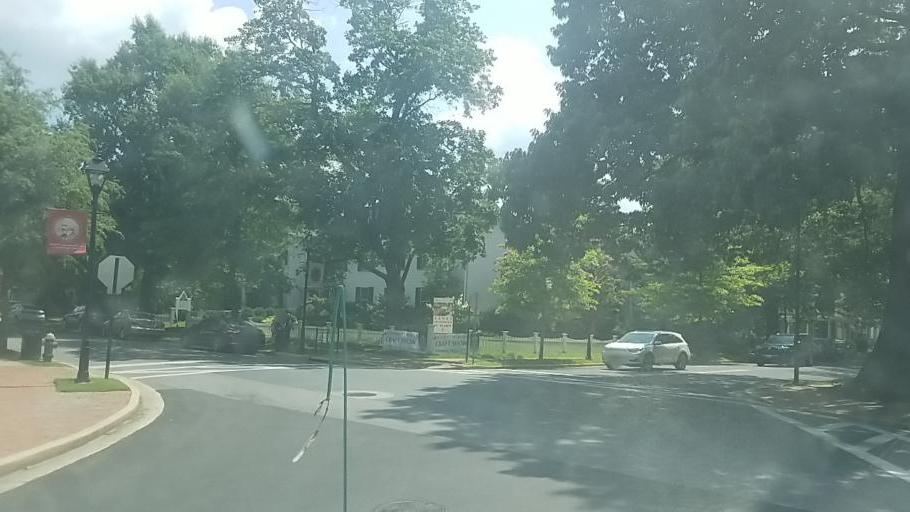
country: US
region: Maryland
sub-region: Talbot County
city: Easton
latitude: 38.7725
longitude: -76.0746
